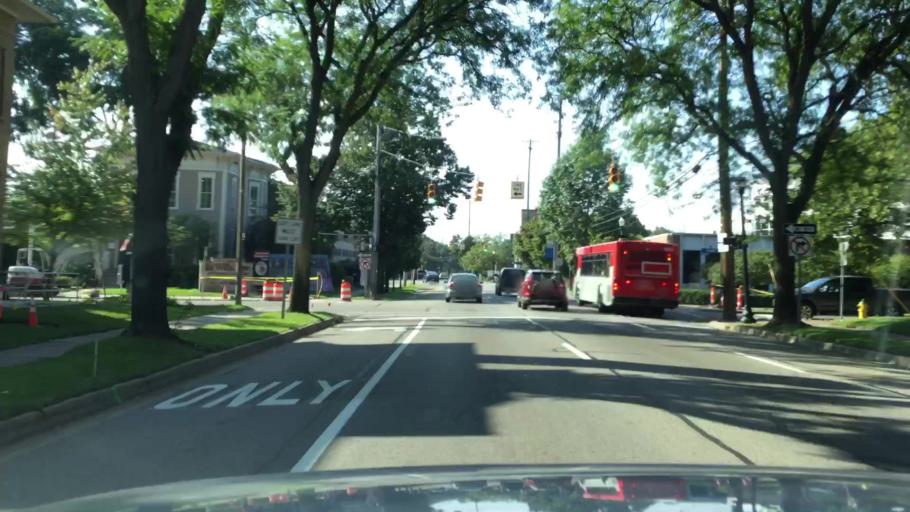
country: US
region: Michigan
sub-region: Kalamazoo County
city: Kalamazoo
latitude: 42.2900
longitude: -85.5897
